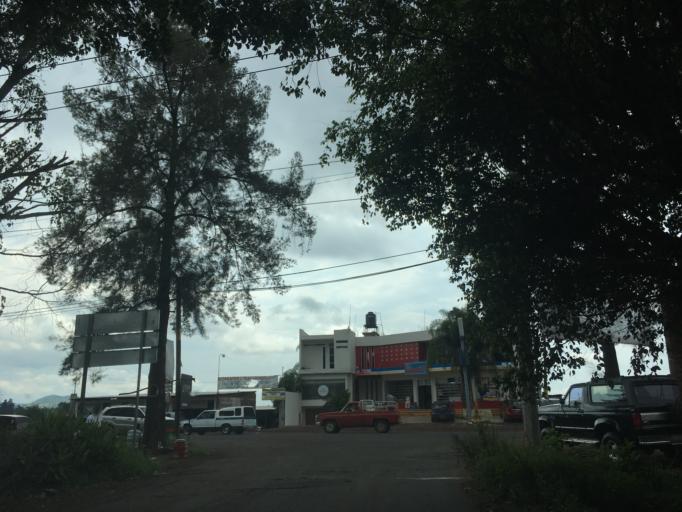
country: MX
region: Michoacan
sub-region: Periban
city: Gildardo Magana (Los Angeles)
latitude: 19.5741
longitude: -102.4585
